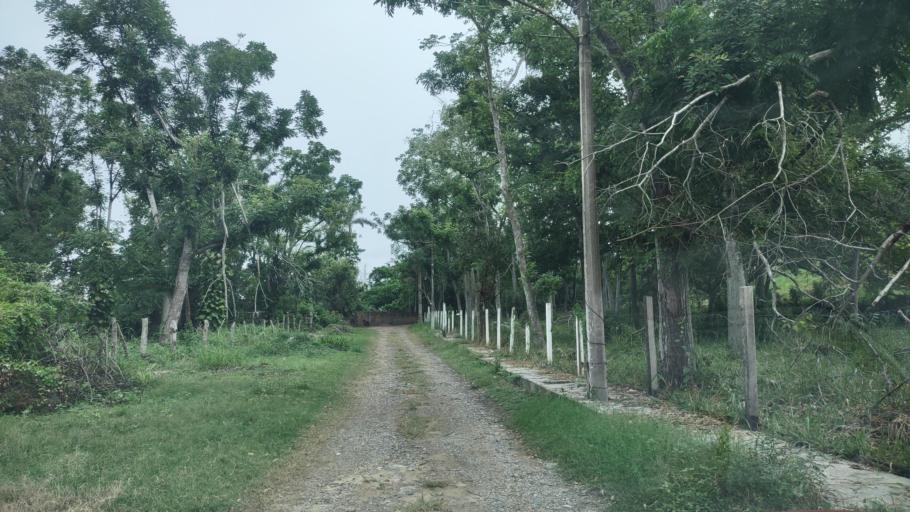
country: MX
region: Veracruz
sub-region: Papantla
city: Fraccionamiento la Florida
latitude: 20.5877
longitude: -97.4222
